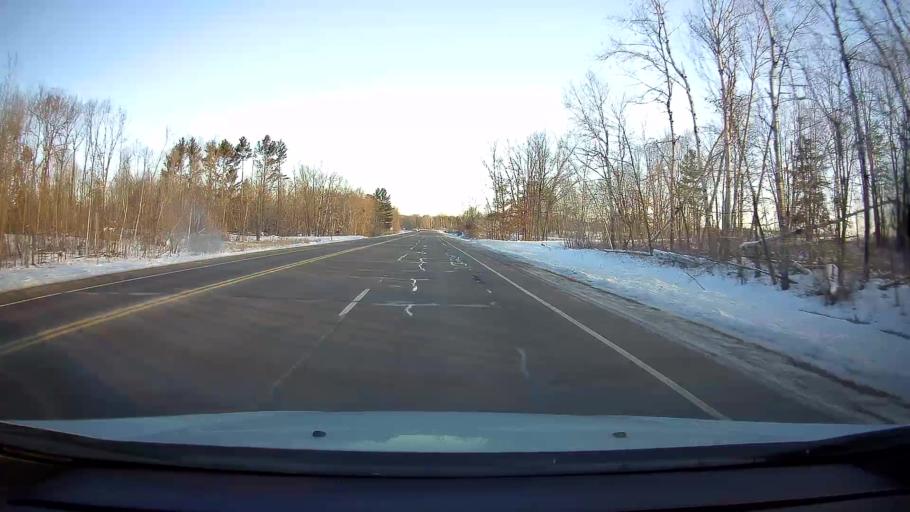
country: US
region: Wisconsin
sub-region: Barron County
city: Turtle Lake
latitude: 45.4260
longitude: -92.1297
